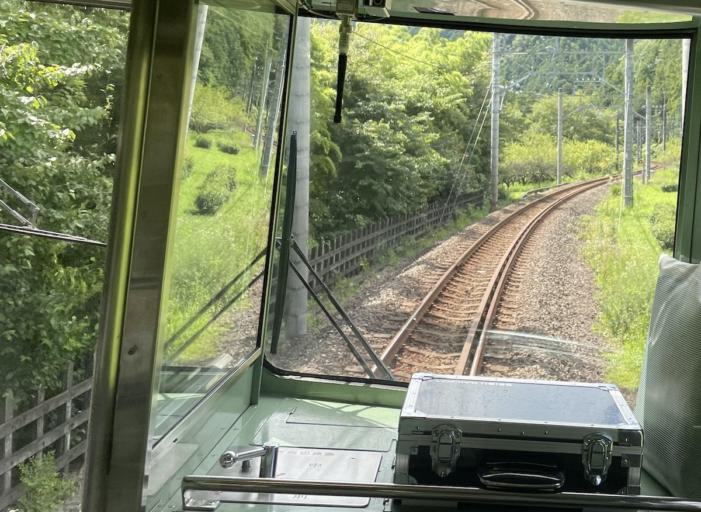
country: JP
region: Saitama
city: Morohongo
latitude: 35.8901
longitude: 139.2690
